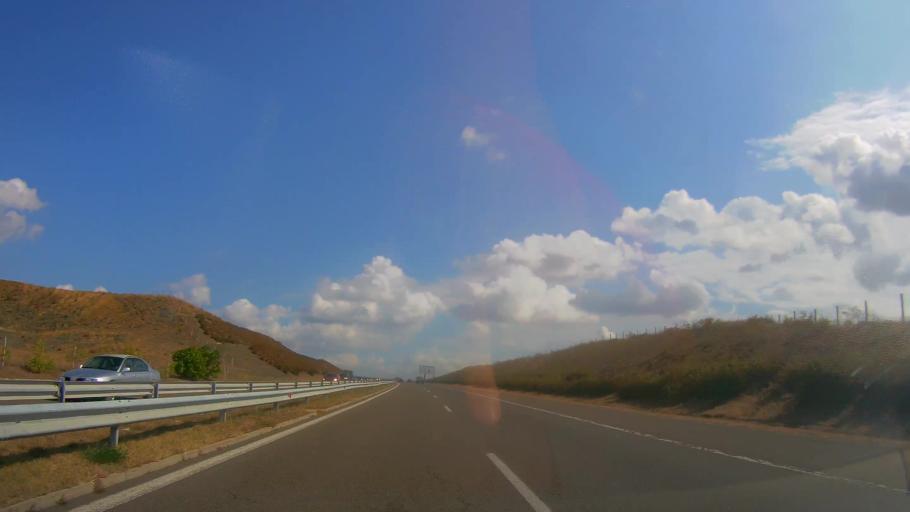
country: BG
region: Burgas
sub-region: Obshtina Kameno
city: Kameno
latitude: 42.5921
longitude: 27.1759
